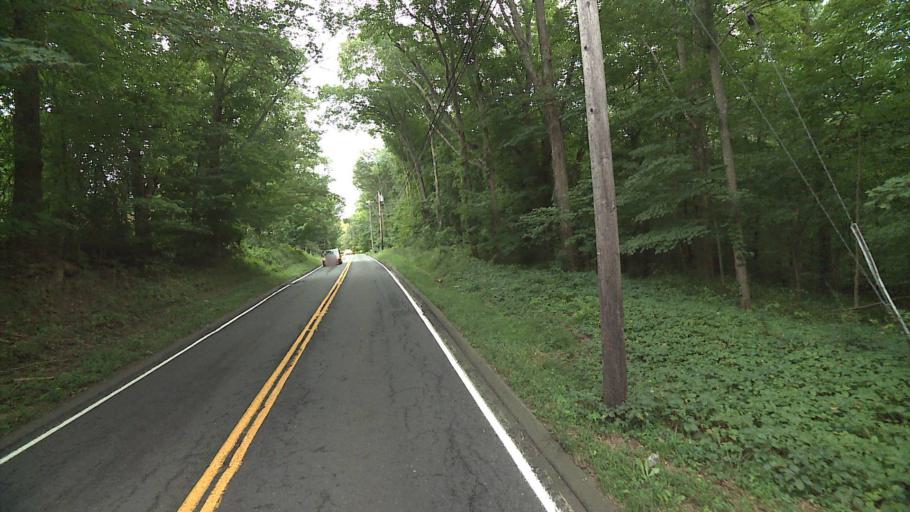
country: US
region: Connecticut
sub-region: Hartford County
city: Manchester
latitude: 41.7968
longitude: -72.4733
